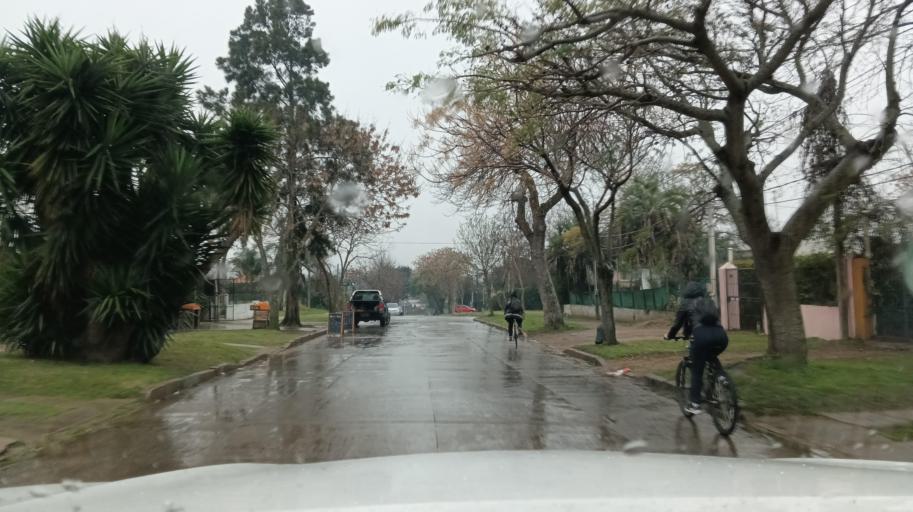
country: UY
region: Canelones
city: Paso de Carrasco
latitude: -34.8753
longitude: -56.0873
